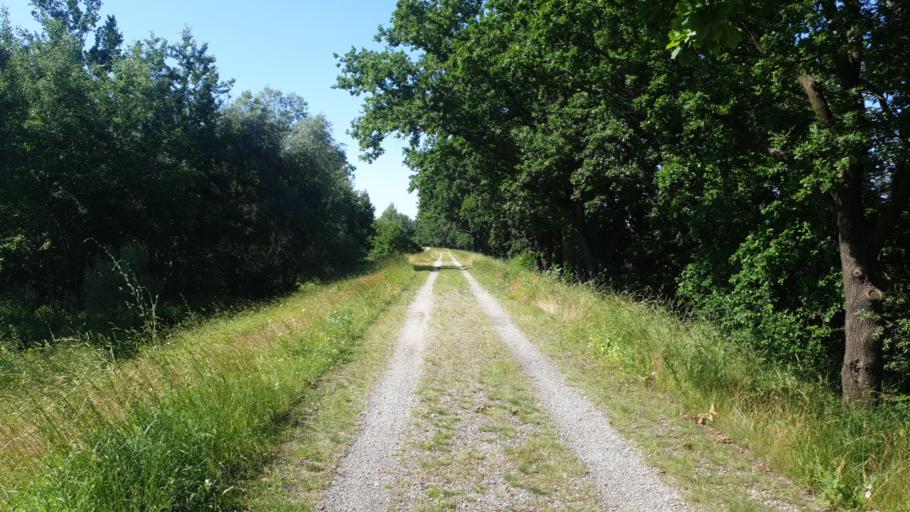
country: PL
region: Lower Silesian Voivodeship
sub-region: Powiat wroclawski
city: Radwanice
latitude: 51.0899
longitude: 17.1158
